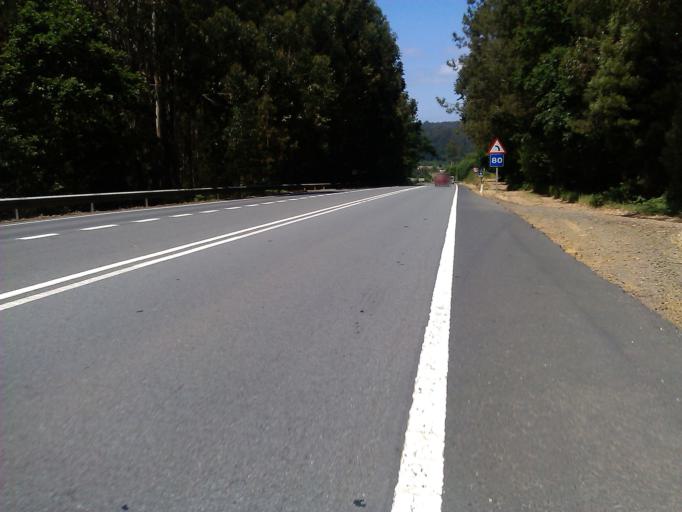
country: ES
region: Galicia
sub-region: Provincia da Coruna
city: Touro
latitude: 42.9167
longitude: -8.3457
